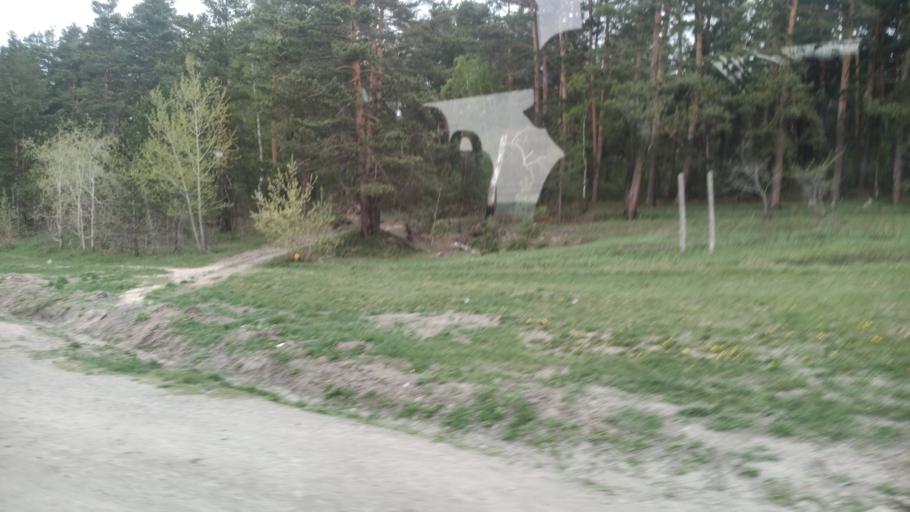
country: RU
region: Altai Krai
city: Yuzhnyy
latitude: 53.2665
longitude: 83.7185
